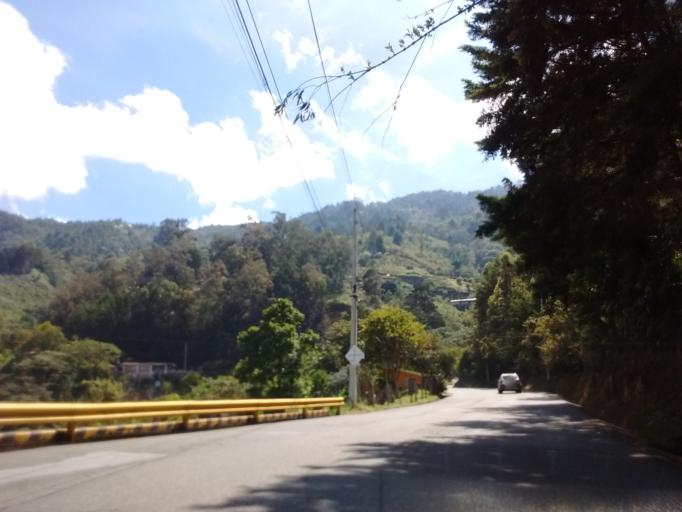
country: CO
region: Antioquia
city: Medellin
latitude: 6.2390
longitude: -75.5180
